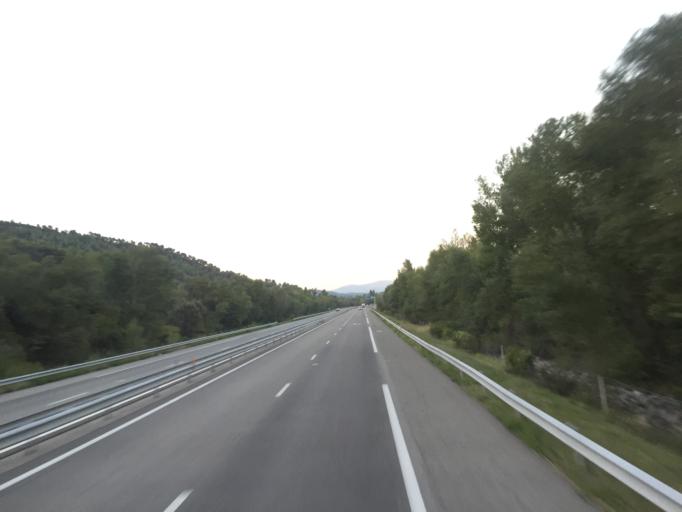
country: FR
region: Provence-Alpes-Cote d'Azur
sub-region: Departement des Alpes-de-Haute-Provence
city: Peyruis
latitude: 43.9945
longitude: 5.9181
